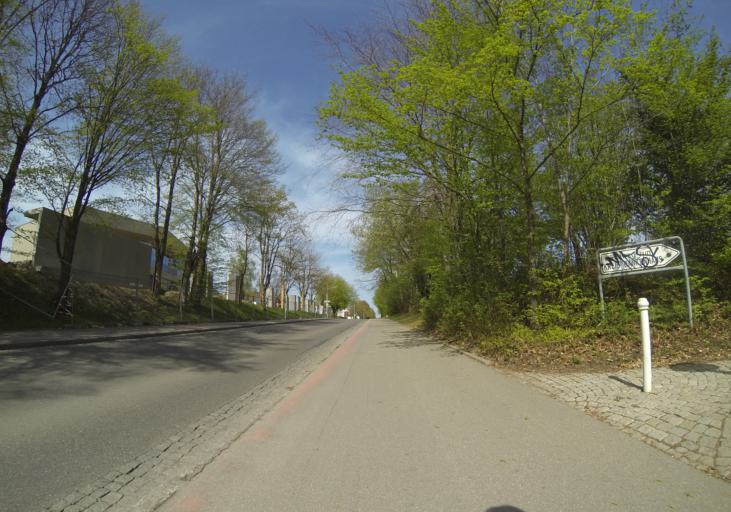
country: DE
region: Baden-Wuerttemberg
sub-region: Tuebingen Region
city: Laupheim
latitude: 48.2338
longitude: 9.8874
